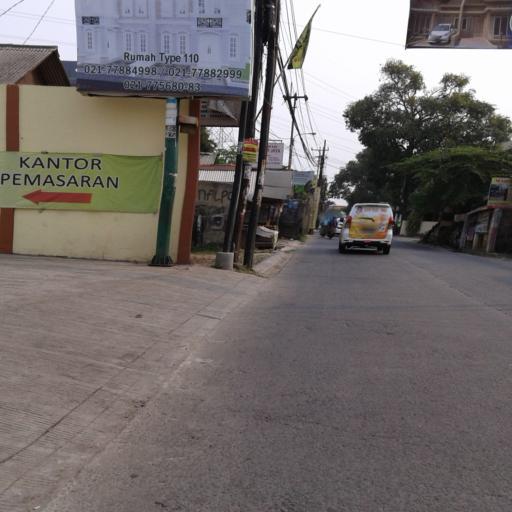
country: ID
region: West Java
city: Sawangan
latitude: -6.3729
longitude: 106.7724
